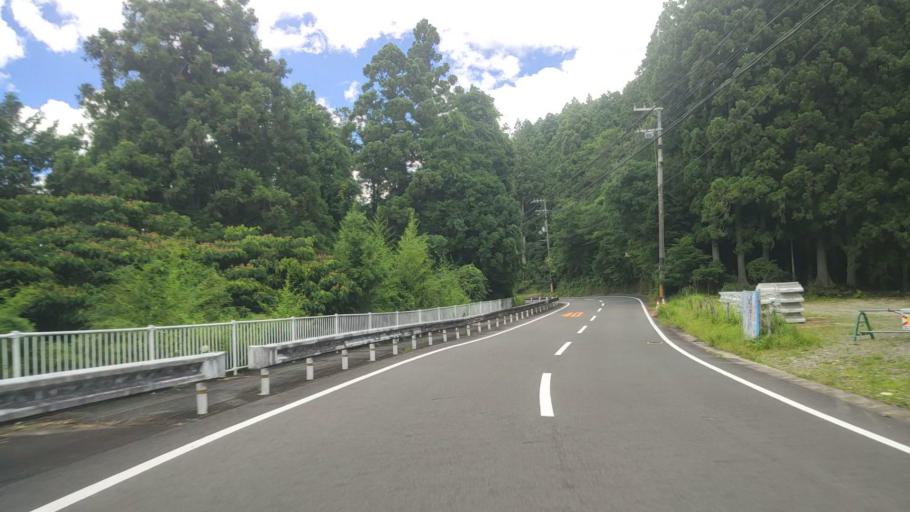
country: JP
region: Mie
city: Owase
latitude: 33.9533
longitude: 136.0687
